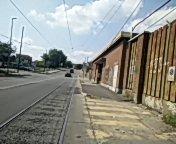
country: IT
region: Piedmont
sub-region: Provincia di Torino
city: Nichelino
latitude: 45.0228
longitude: 7.6599
